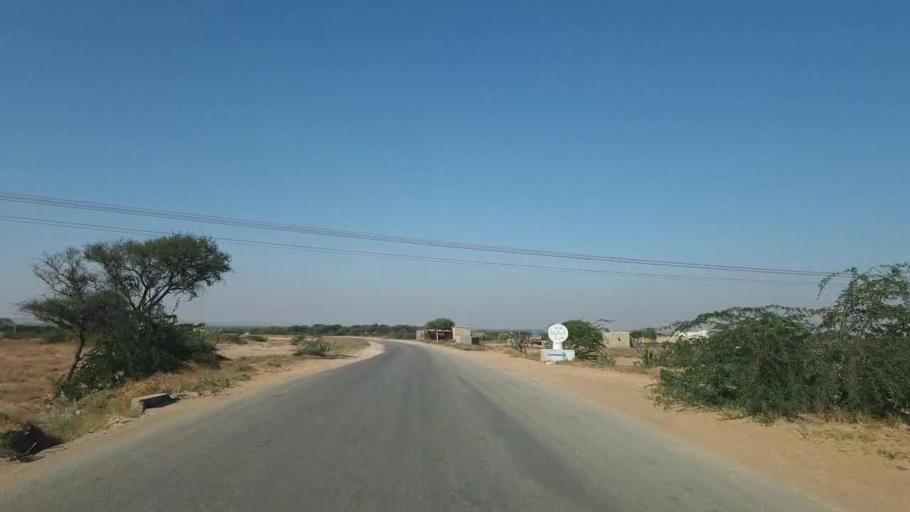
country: PK
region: Sindh
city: Gharo
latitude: 25.1882
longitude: 67.6567
